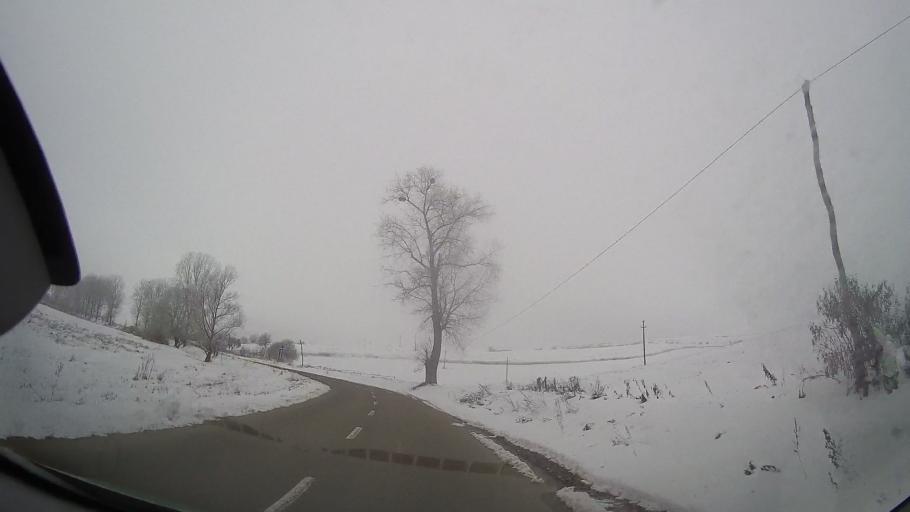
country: RO
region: Neamt
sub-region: Comuna Oniceni
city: Oniceni
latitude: 46.8021
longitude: 27.1339
